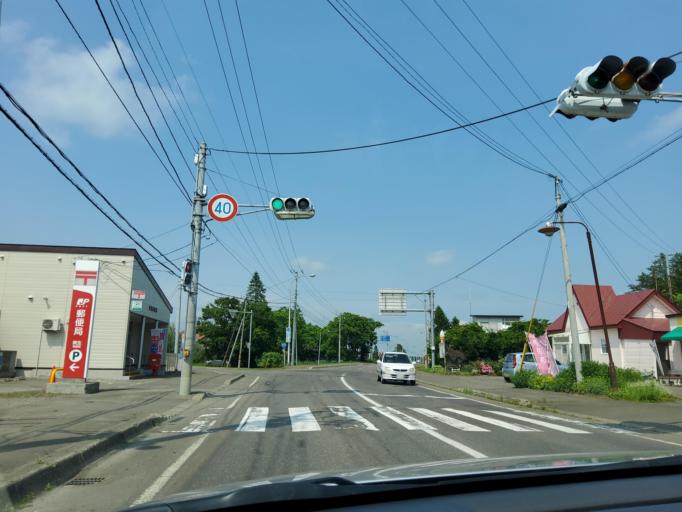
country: JP
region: Hokkaido
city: Obihiro
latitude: 42.8656
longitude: 143.0156
